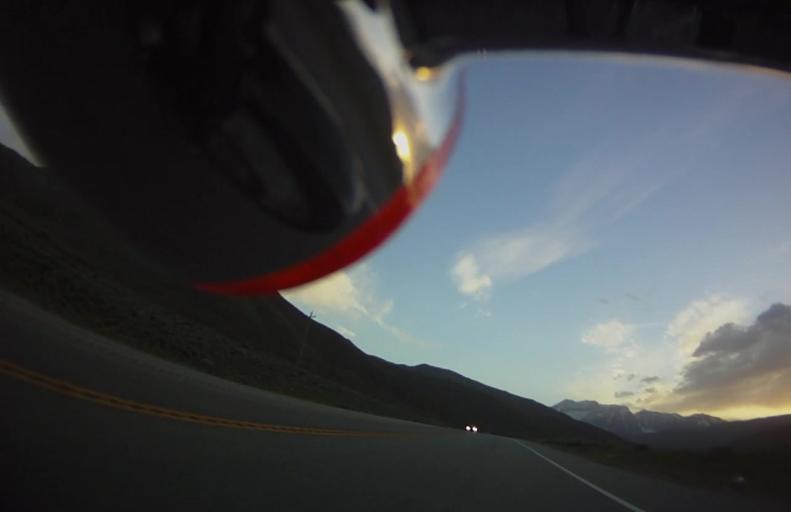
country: US
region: Utah
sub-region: Wasatch County
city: Midway
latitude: 40.4086
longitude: -111.4817
